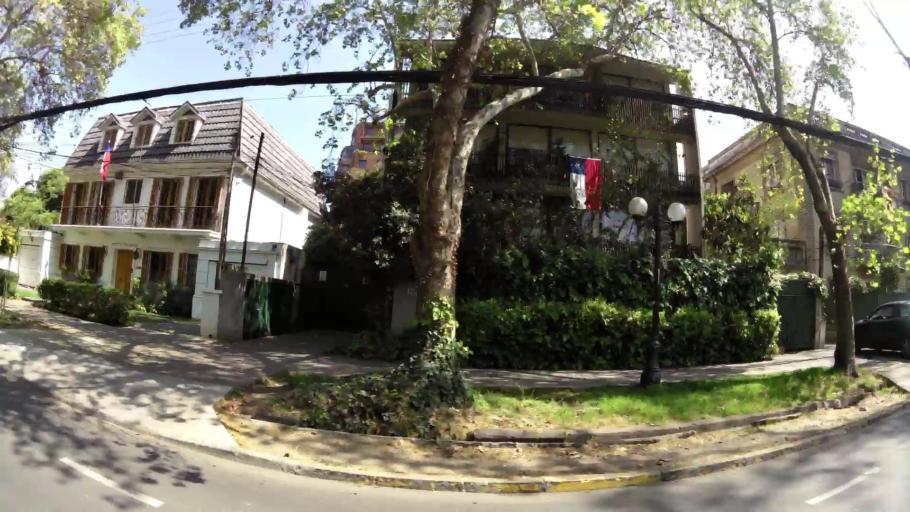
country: CL
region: Santiago Metropolitan
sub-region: Provincia de Santiago
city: Villa Presidente Frei, Nunoa, Santiago, Chile
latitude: -33.4311
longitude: -70.6064
